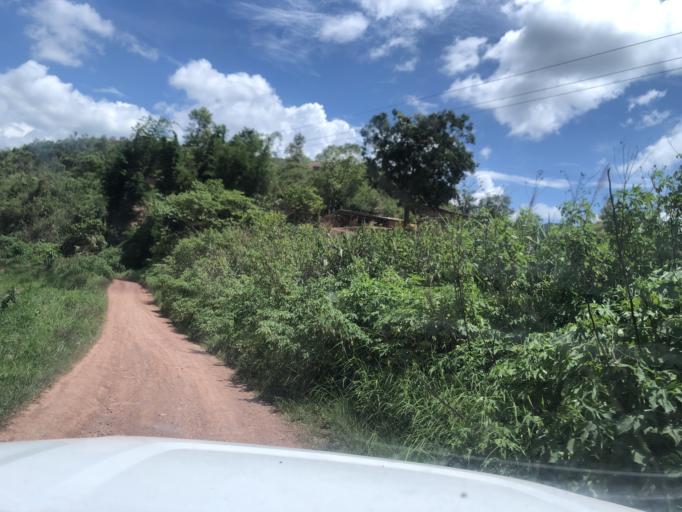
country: CN
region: Yunnan
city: Menglie
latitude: 22.2487
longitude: 101.6061
